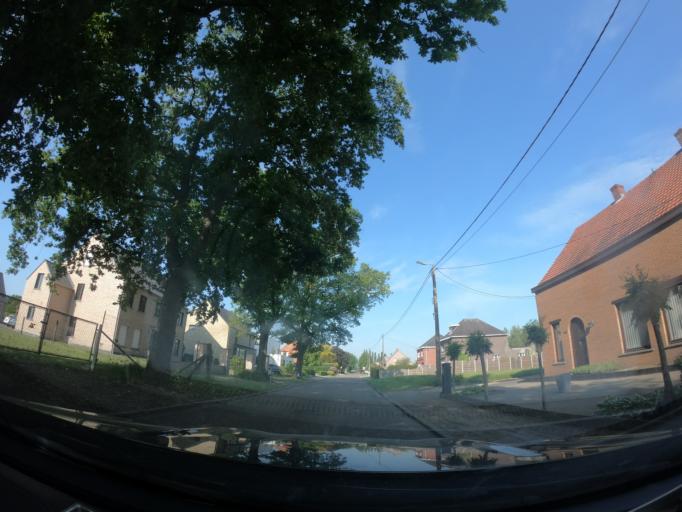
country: BE
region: Flanders
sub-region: Provincie Antwerpen
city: Hulshout
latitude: 51.1187
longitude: 4.8113
